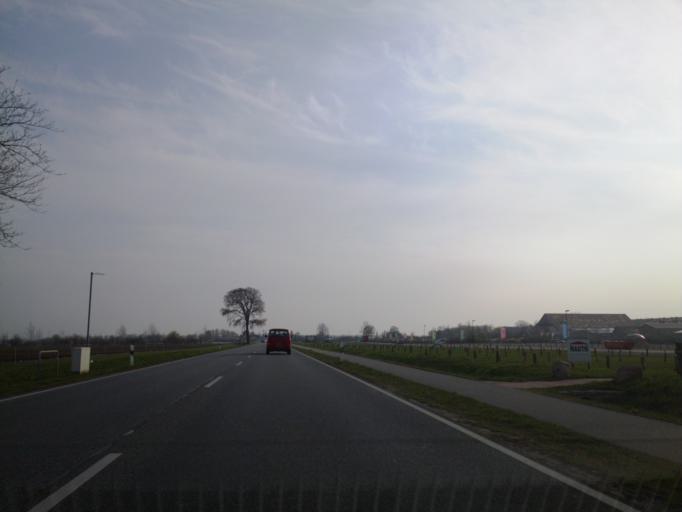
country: DE
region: Mecklenburg-Vorpommern
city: Rovershagen
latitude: 54.1633
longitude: 12.2357
